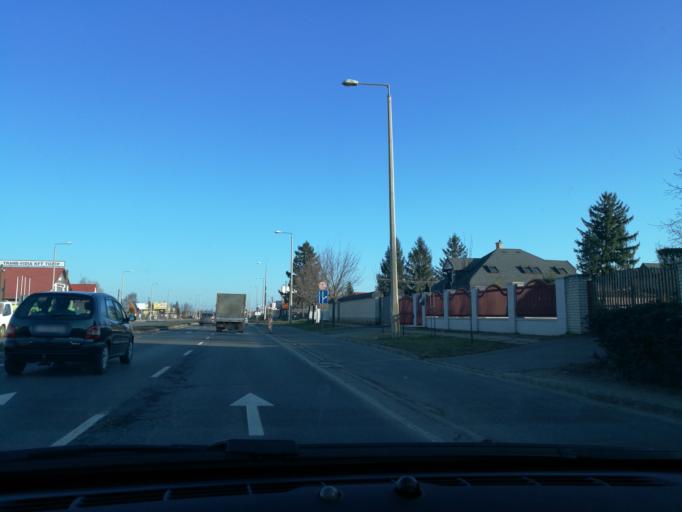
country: HU
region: Szabolcs-Szatmar-Bereg
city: Nyiregyhaza
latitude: 47.9509
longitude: 21.7637
